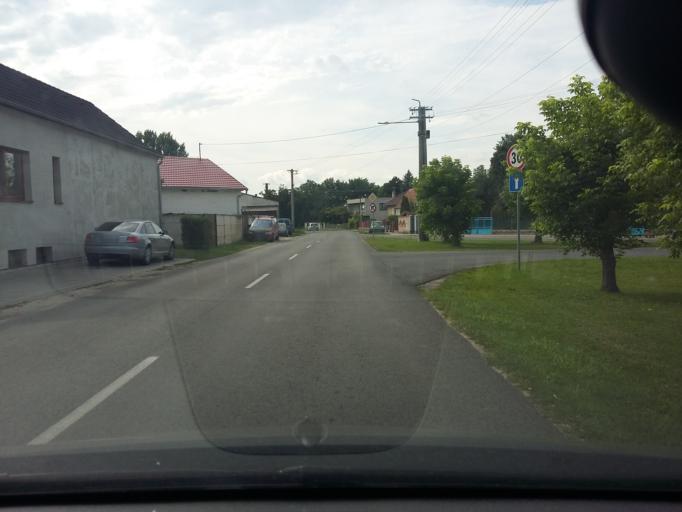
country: SK
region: Trnavsky
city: Gbely
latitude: 48.6275
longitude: 17.2019
